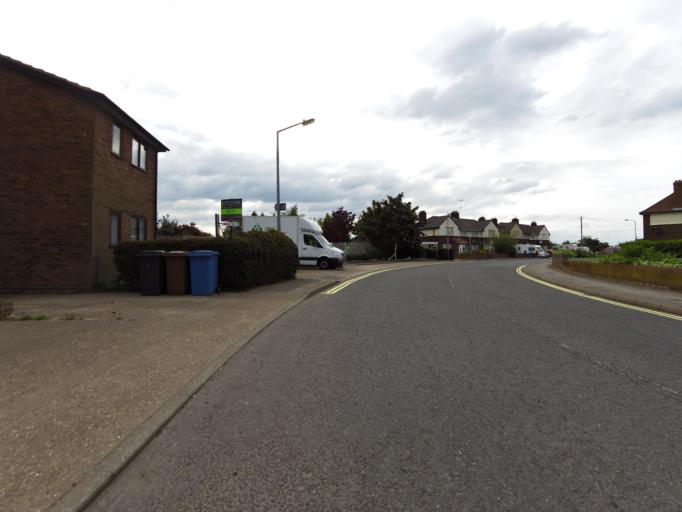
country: GB
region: England
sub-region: Suffolk
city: Ipswich
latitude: 52.0366
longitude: 1.1664
